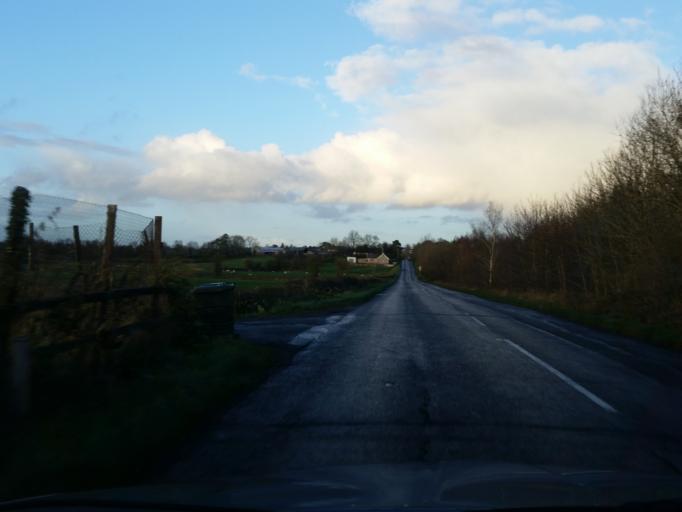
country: GB
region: Northern Ireland
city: Lisnaskea
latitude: 54.2355
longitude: -7.4533
